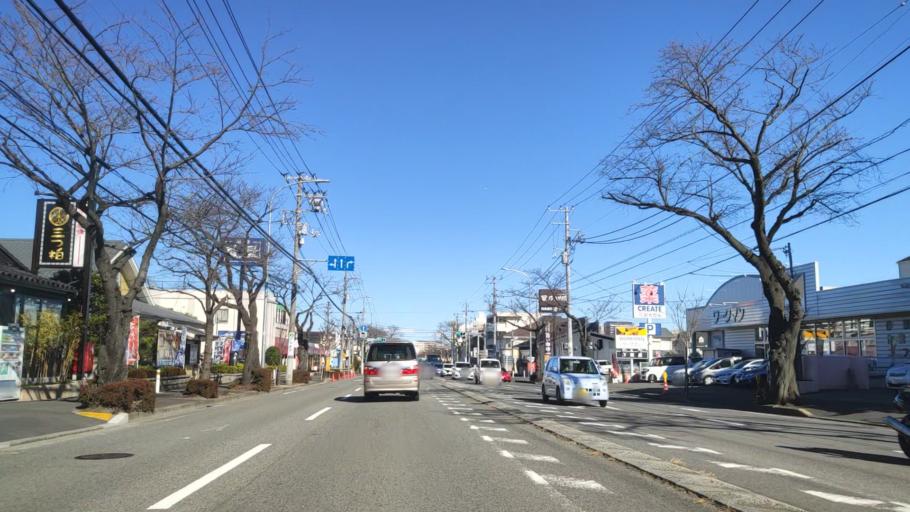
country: JP
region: Tokyo
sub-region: Machida-shi
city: Machida
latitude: 35.5173
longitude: 139.5021
